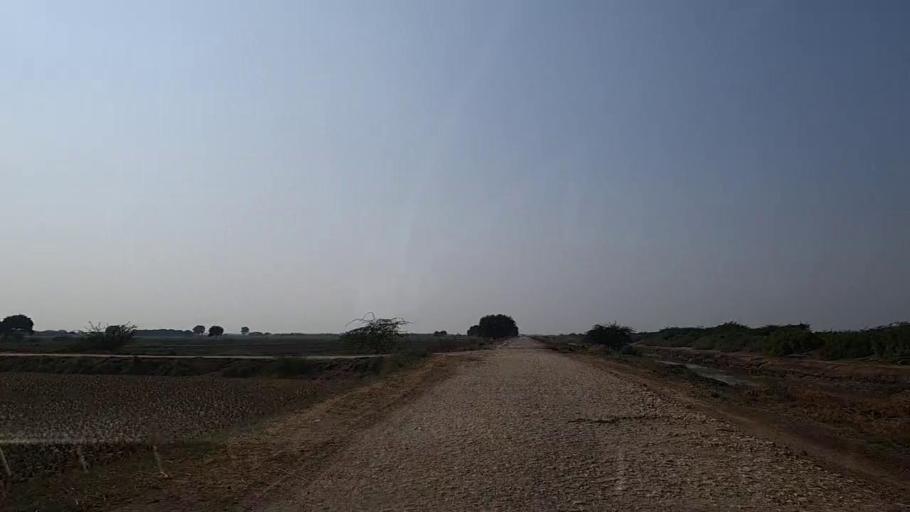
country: PK
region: Sindh
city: Mirpur Sakro
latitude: 24.6365
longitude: 67.7308
